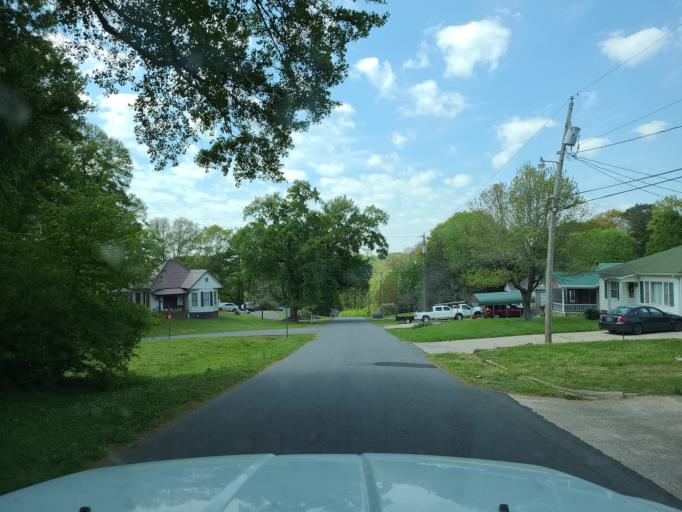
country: US
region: North Carolina
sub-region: Lincoln County
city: Lincolnton
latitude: 35.4709
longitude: -81.2661
